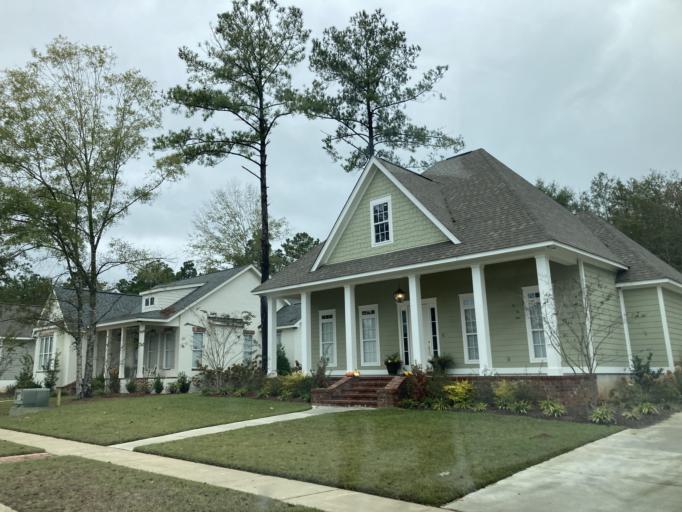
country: US
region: Mississippi
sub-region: Lamar County
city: West Hattiesburg
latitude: 31.2876
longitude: -89.4774
